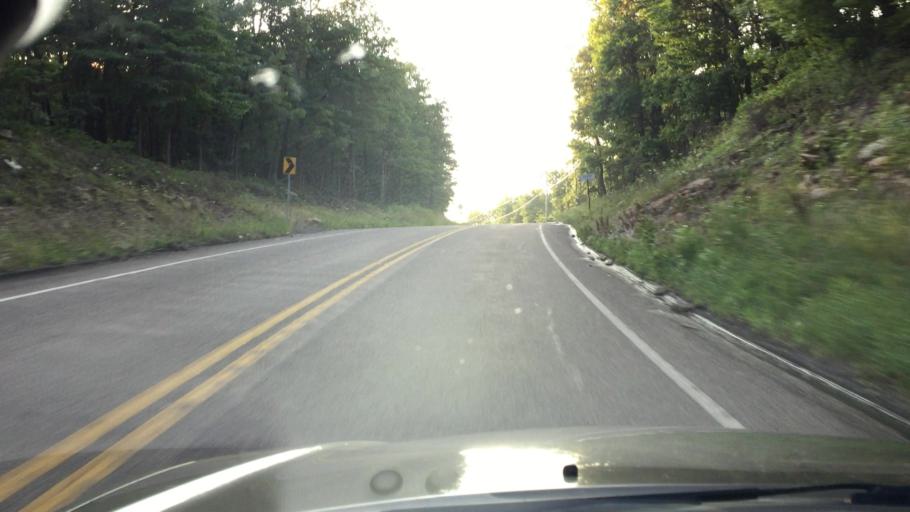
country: US
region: Pennsylvania
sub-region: Carbon County
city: Weatherly
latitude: 40.9261
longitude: -75.8912
